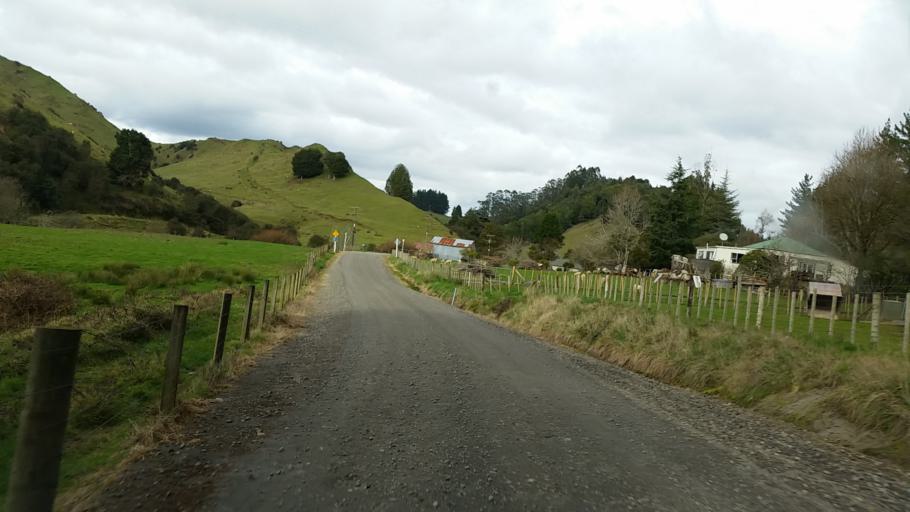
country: NZ
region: Taranaki
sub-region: New Plymouth District
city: Waitara
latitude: -39.1576
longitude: 174.5615
